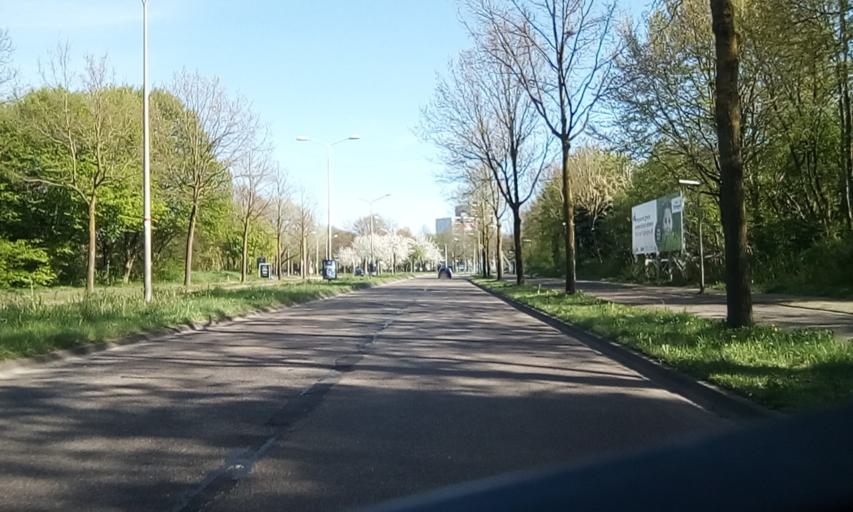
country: NL
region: Gelderland
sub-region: Gemeente Nijmegen
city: Lindenholt
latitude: 51.8183
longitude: 5.7990
